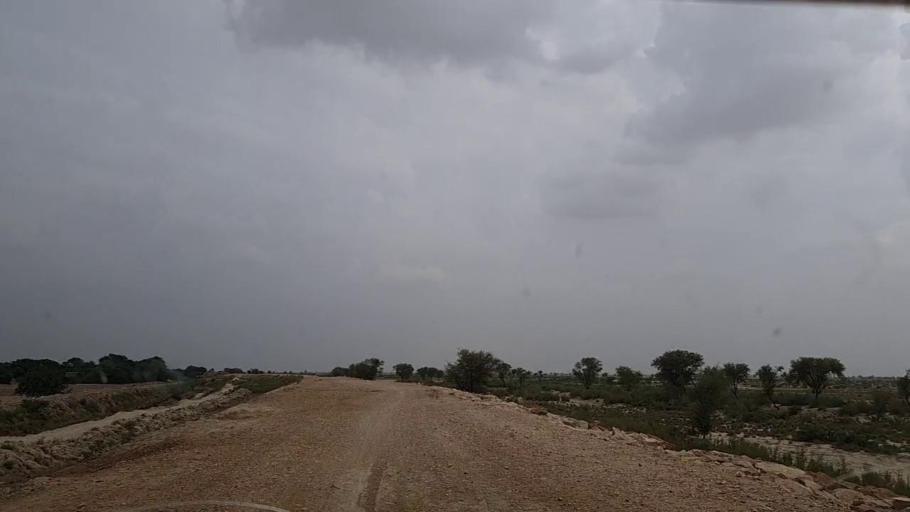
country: PK
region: Sindh
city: Johi
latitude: 26.7238
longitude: 67.5783
